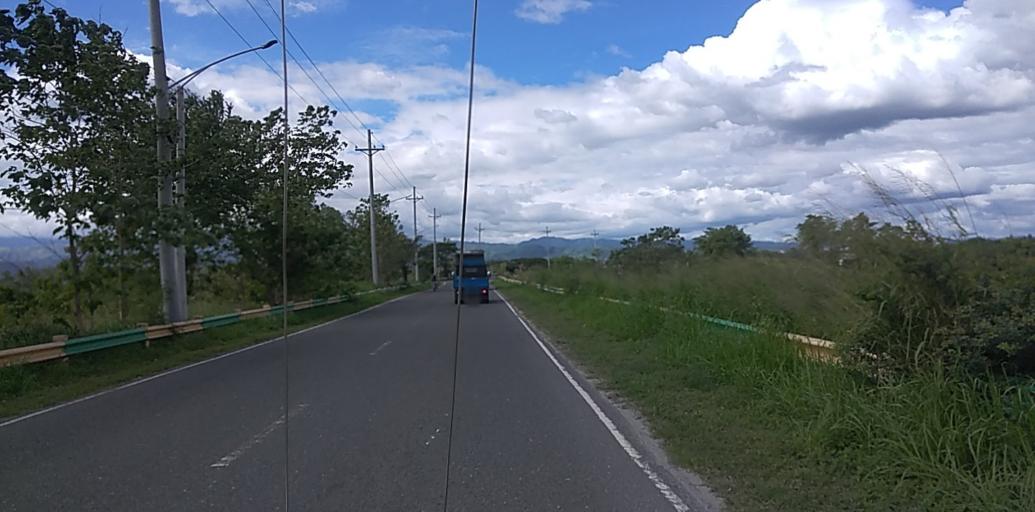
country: PH
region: Central Luzon
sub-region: Province of Pampanga
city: Porac
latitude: 15.0860
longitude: 120.5413
